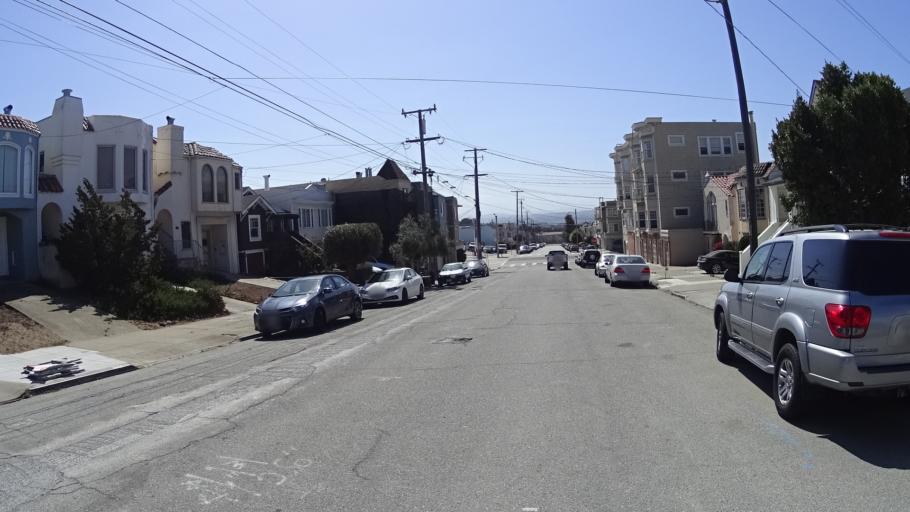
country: US
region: California
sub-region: San Mateo County
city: Daly City
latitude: 37.7434
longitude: -122.4865
